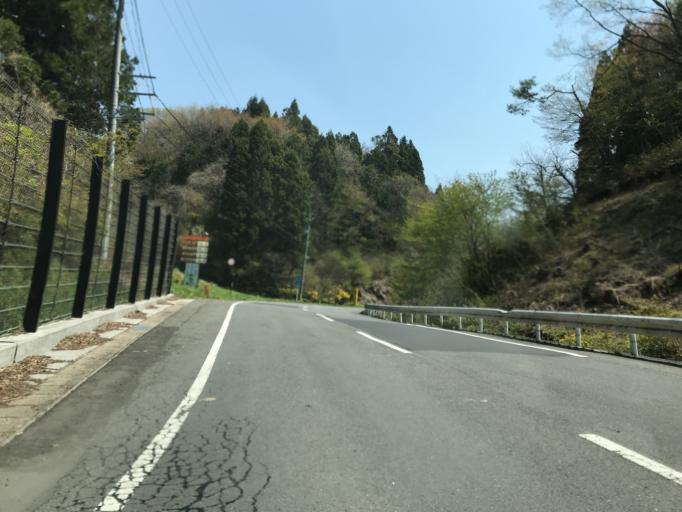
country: JP
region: Fukushima
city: Ishikawa
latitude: 37.0673
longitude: 140.4352
